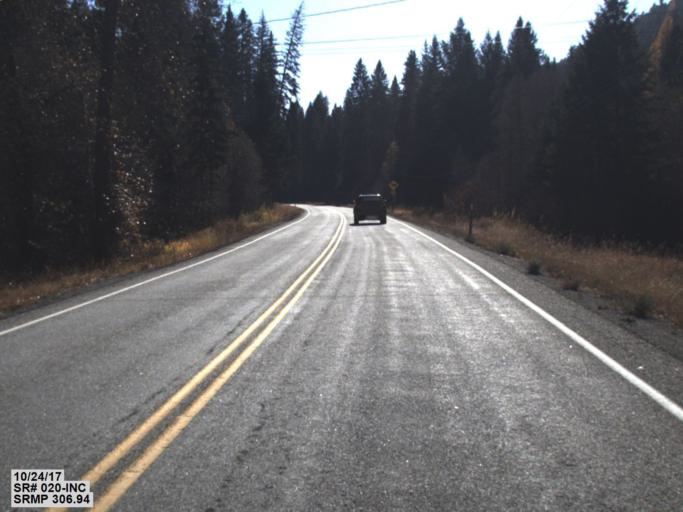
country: US
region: Washington
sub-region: Ferry County
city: Republic
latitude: 48.6281
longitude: -118.6761
